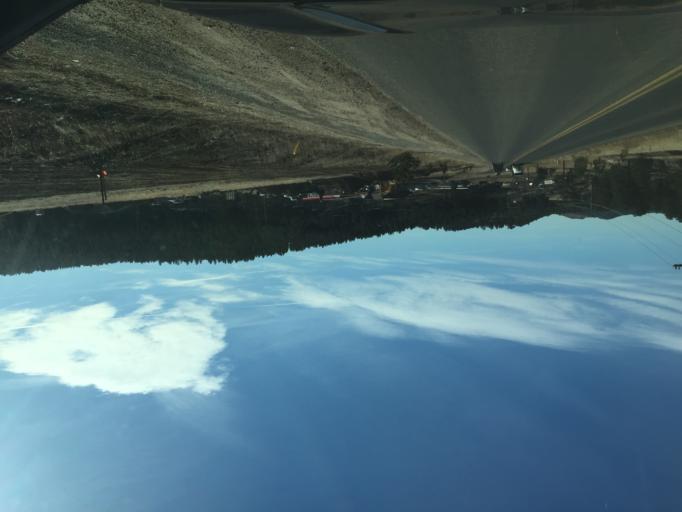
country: US
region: Colorado
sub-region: Jefferson County
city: Evergreen
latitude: 39.4413
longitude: -105.4567
